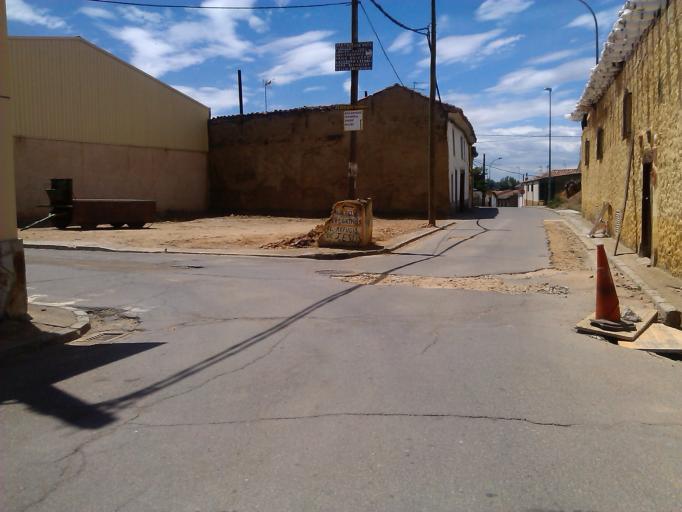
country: ES
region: Castille and Leon
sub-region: Provincia de Leon
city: Chozas de Abajo
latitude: 42.4843
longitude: -5.7263
